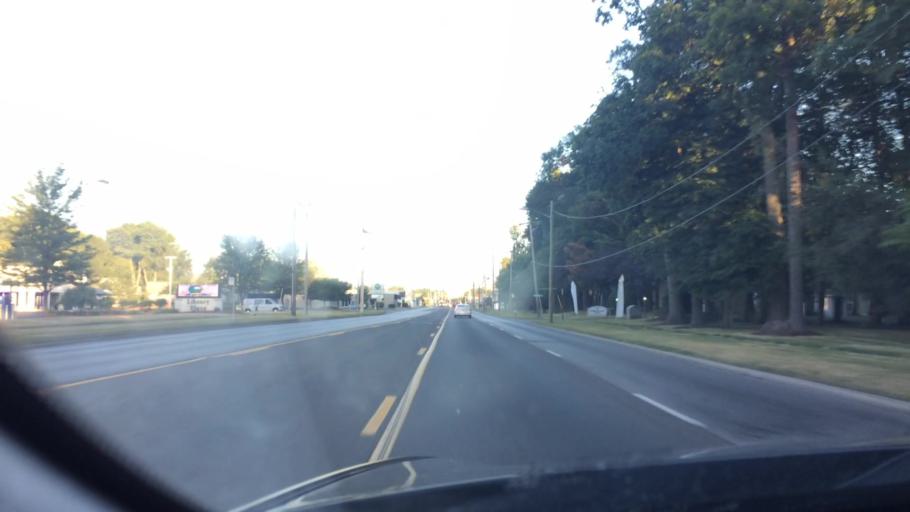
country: US
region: Ohio
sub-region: Lucas County
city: Ottawa Hills
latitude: 41.6533
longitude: -83.6576
